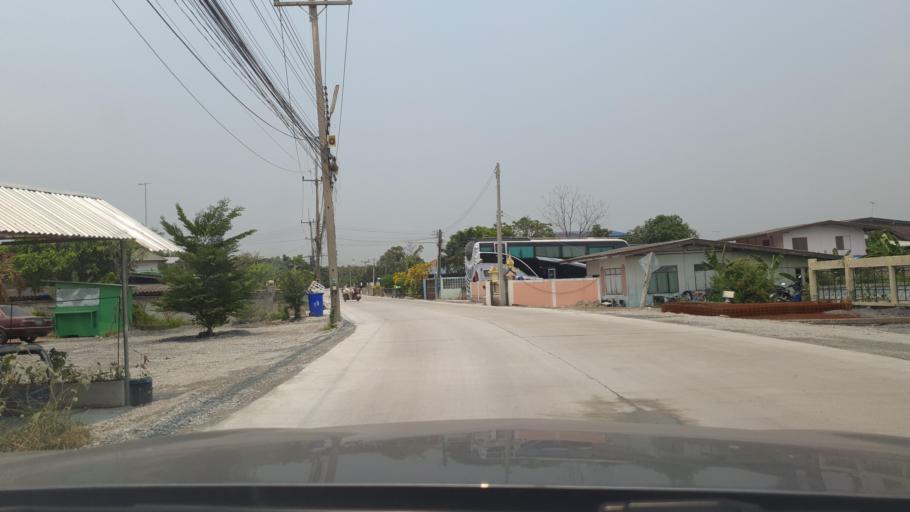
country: TH
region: Chachoengsao
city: Bang Pakong
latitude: 13.4813
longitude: 101.0081
